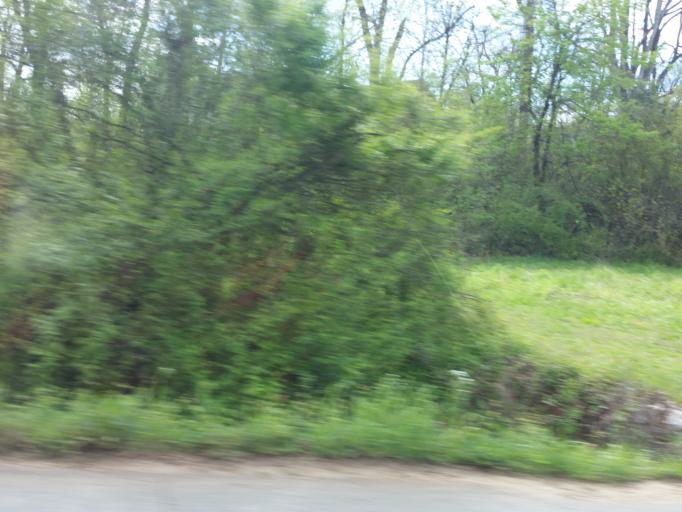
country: US
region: Missouri
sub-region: Butler County
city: Poplar Bluff
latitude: 36.7661
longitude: -90.3910
